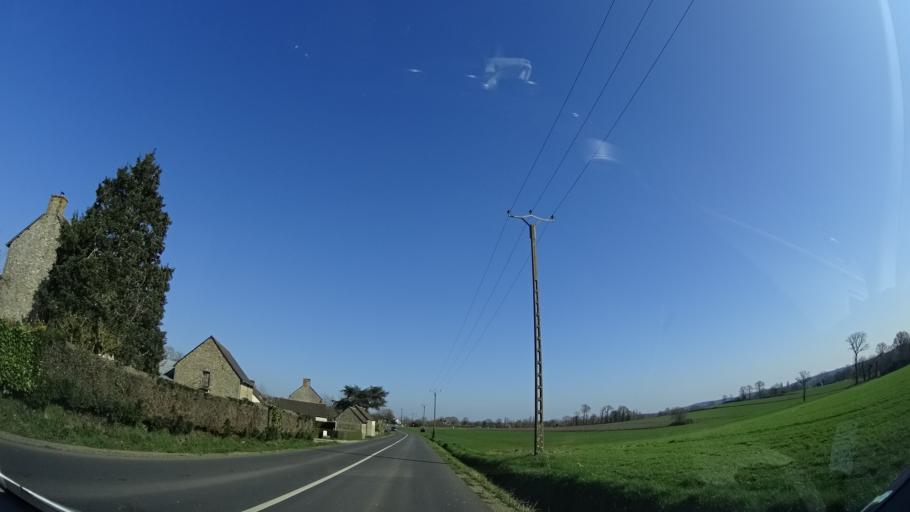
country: FR
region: Brittany
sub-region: Departement d'Ille-et-Vilaine
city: Combourg
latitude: 48.4060
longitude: -1.7699
